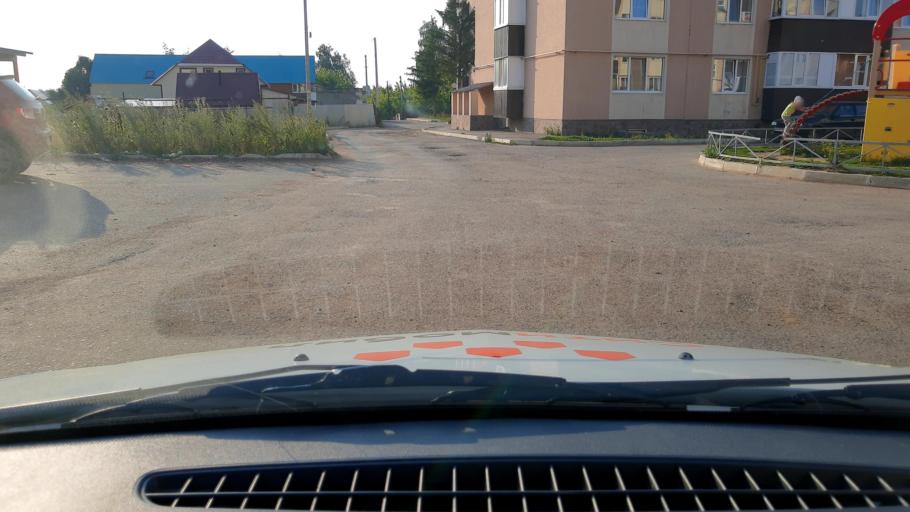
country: RU
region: Bashkortostan
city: Iglino
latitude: 54.8167
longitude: 56.3966
